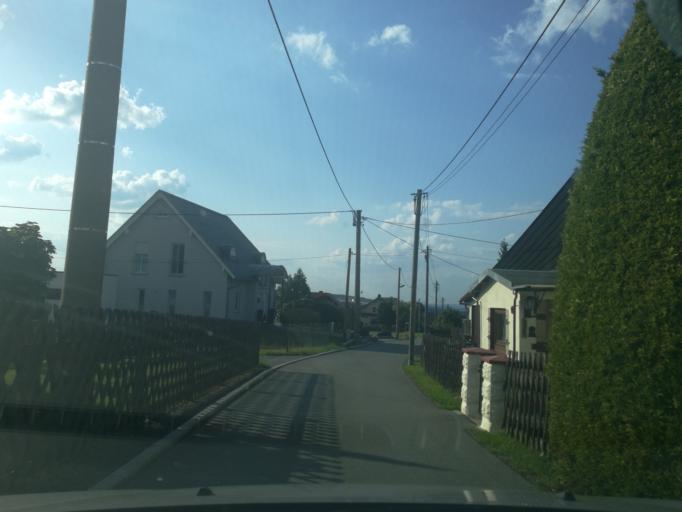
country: DE
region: Saxony
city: Adorf
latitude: 50.3063
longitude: 12.2753
